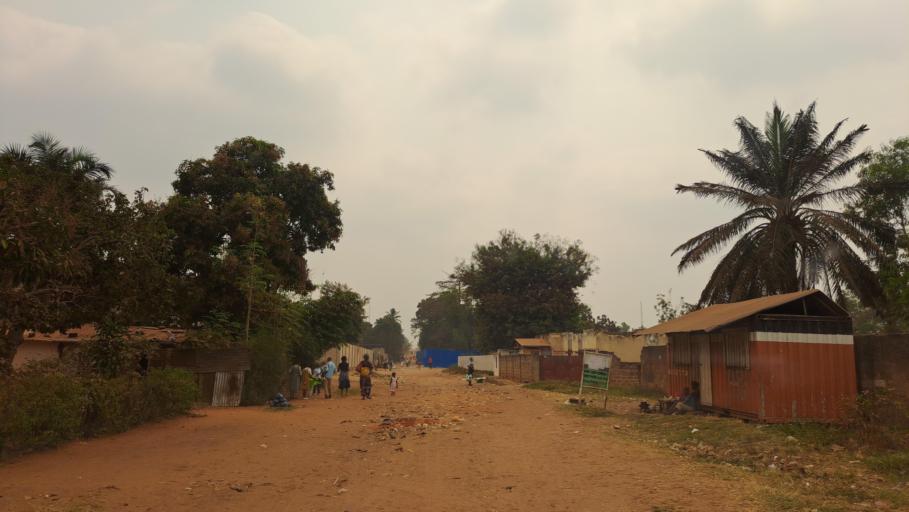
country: CD
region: Kasai-Oriental
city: Mbuji-Mayi
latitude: -6.1156
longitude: 23.6001
